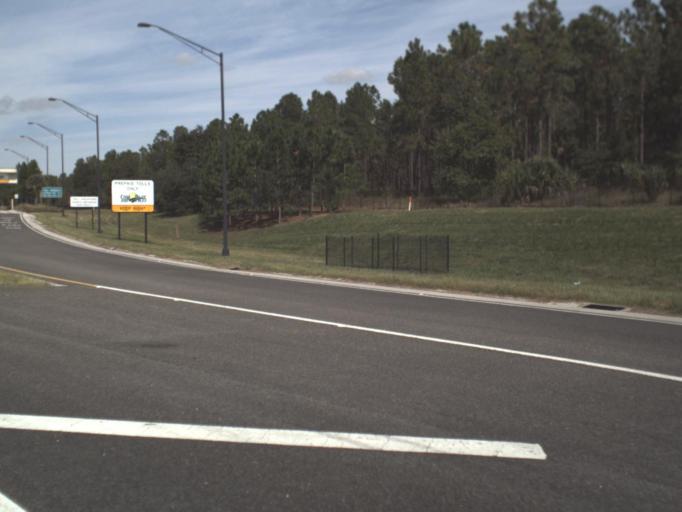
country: US
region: Florida
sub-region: Polk County
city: Citrus Ridge
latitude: 28.2924
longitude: -81.6003
